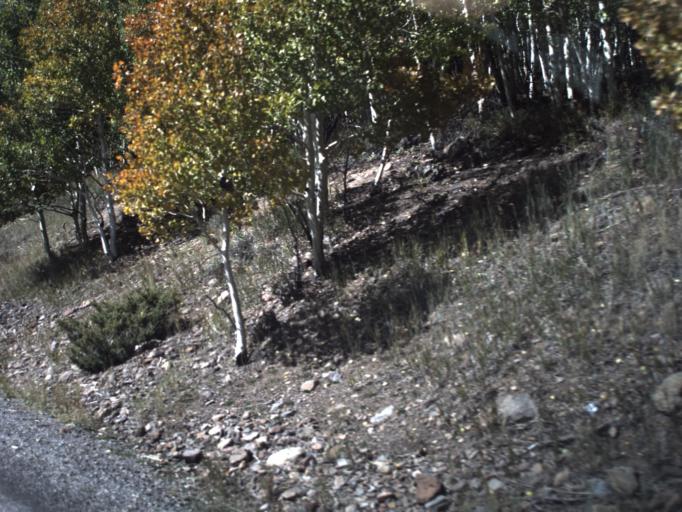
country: US
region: Utah
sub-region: Wayne County
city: Loa
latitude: 38.5380
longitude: -111.7372
